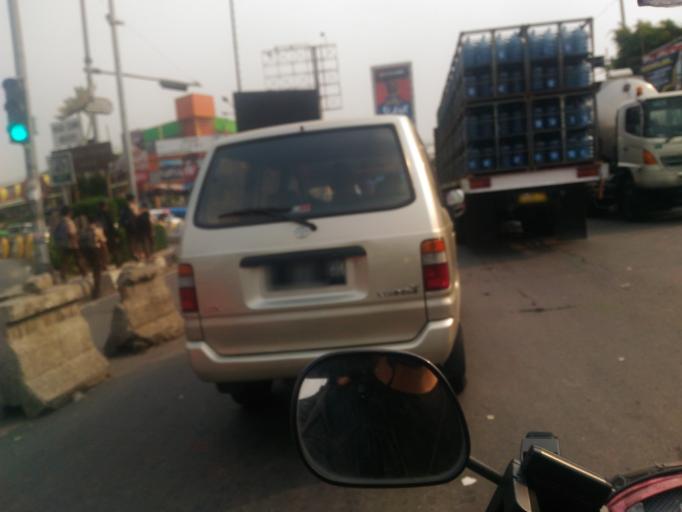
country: ID
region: West Java
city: Caringin
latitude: -6.6555
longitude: 106.8473
